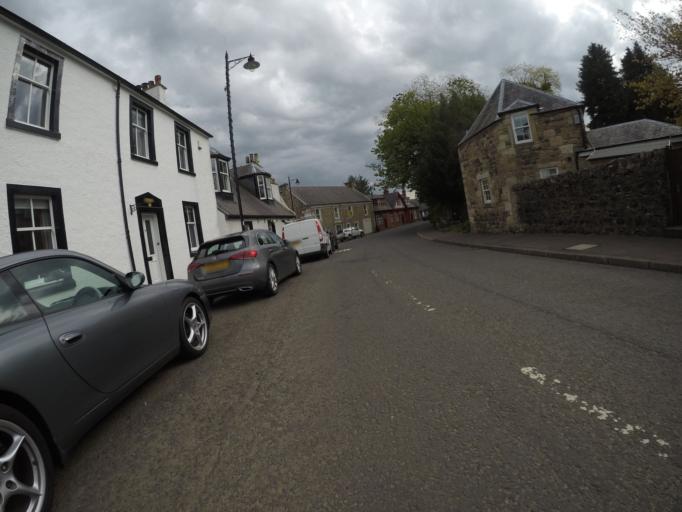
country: GB
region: Scotland
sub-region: East Ayrshire
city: Kilmarnock
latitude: 55.6545
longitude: -4.4457
